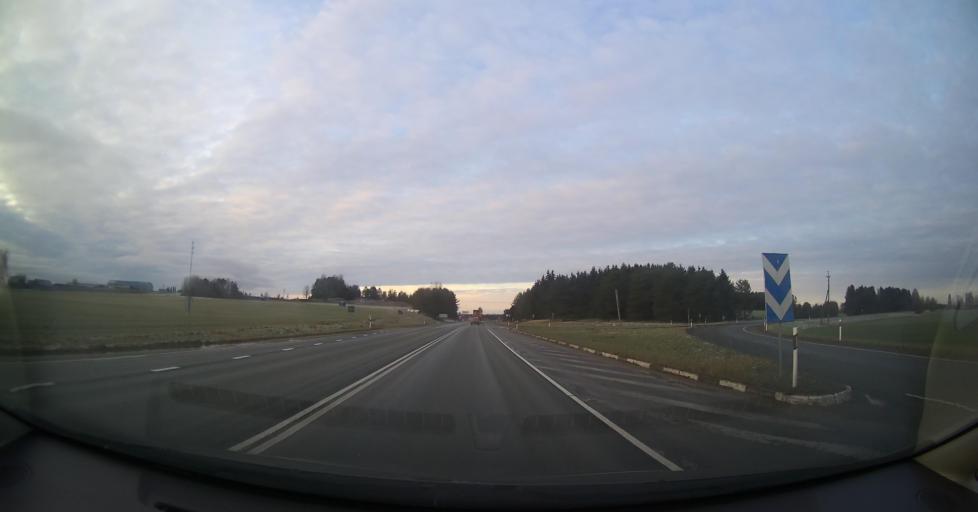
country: EE
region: Tartu
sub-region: Puhja vald
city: Puhja
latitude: 58.4685
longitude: 26.3698
